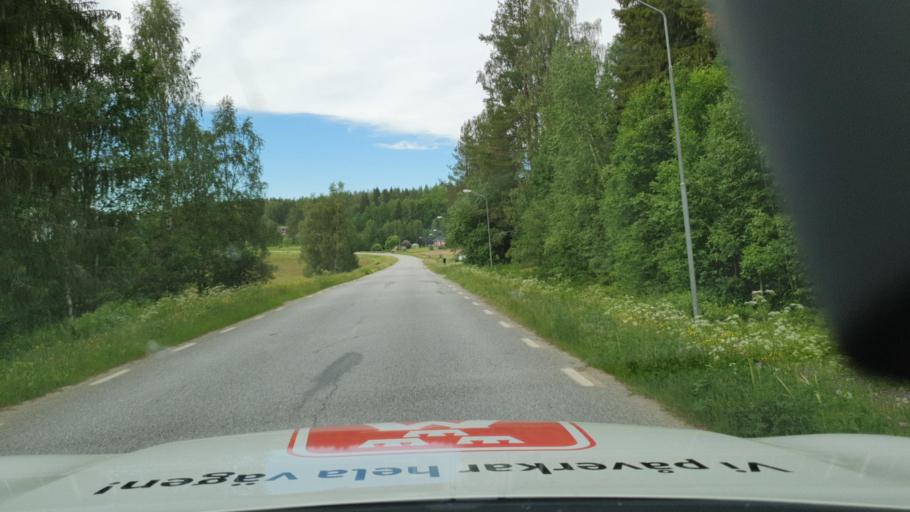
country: SE
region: Vaesterbotten
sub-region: Skelleftea Kommun
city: Burea
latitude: 64.4875
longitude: 21.0347
